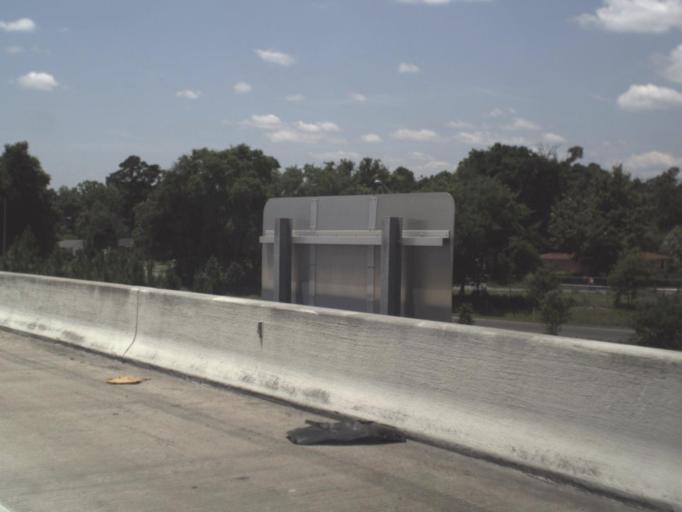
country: US
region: Florida
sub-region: Duval County
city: Jacksonville
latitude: 30.3925
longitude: -81.6681
